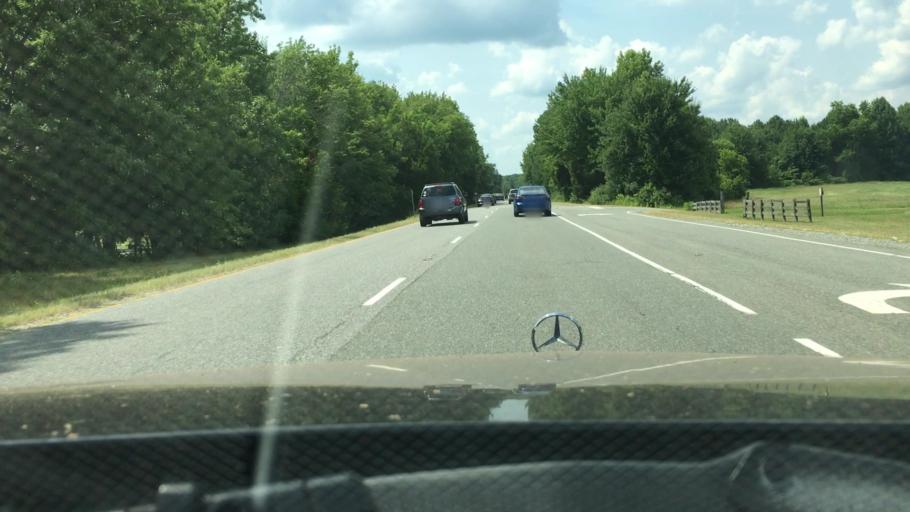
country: US
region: Virginia
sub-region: Spotsylvania County
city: Spotsylvania
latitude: 38.3132
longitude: -77.6821
